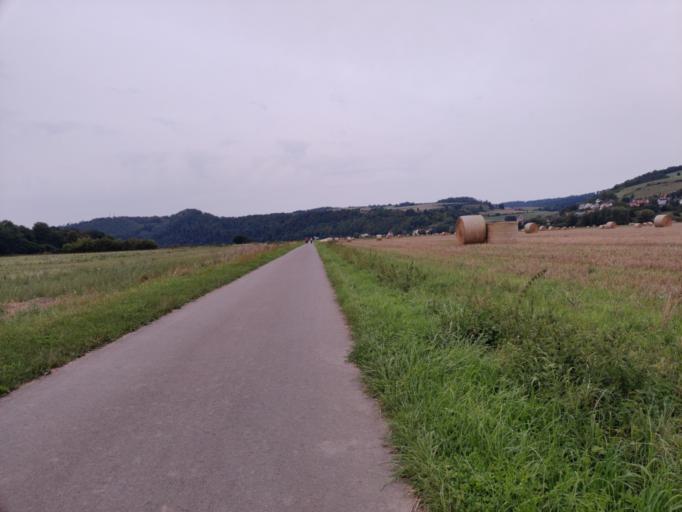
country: DE
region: Lower Saxony
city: Heinsen
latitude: 51.9060
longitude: 9.4381
